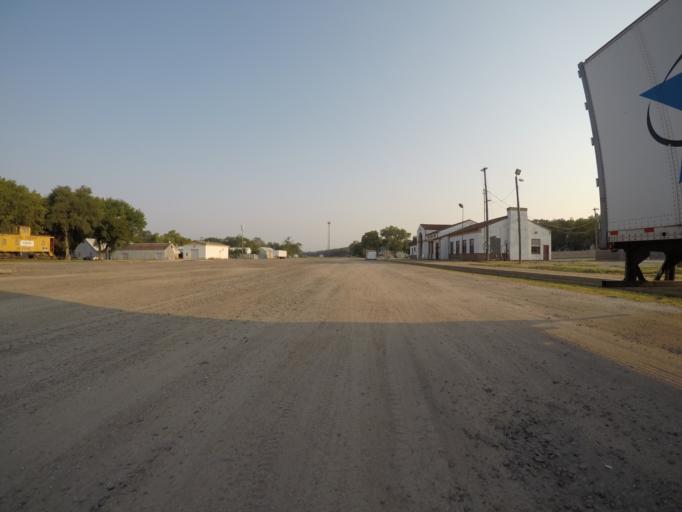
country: US
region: Kansas
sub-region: Marshall County
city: Marysville
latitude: 39.8436
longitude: -96.6493
